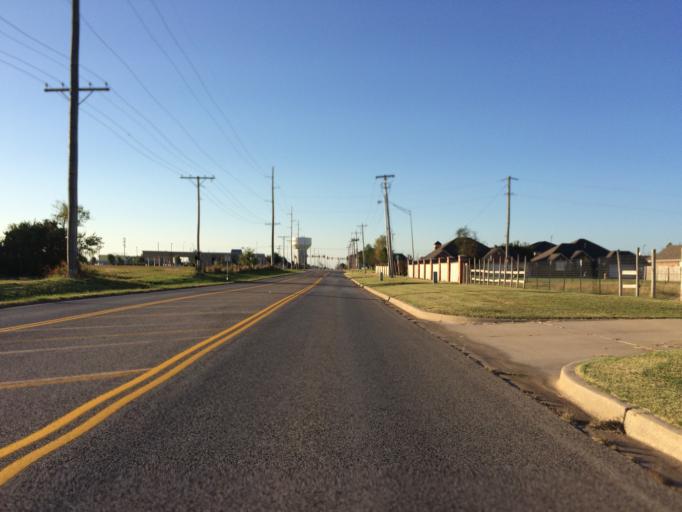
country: US
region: Oklahoma
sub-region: Cleveland County
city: Norman
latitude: 35.2649
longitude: -97.4944
